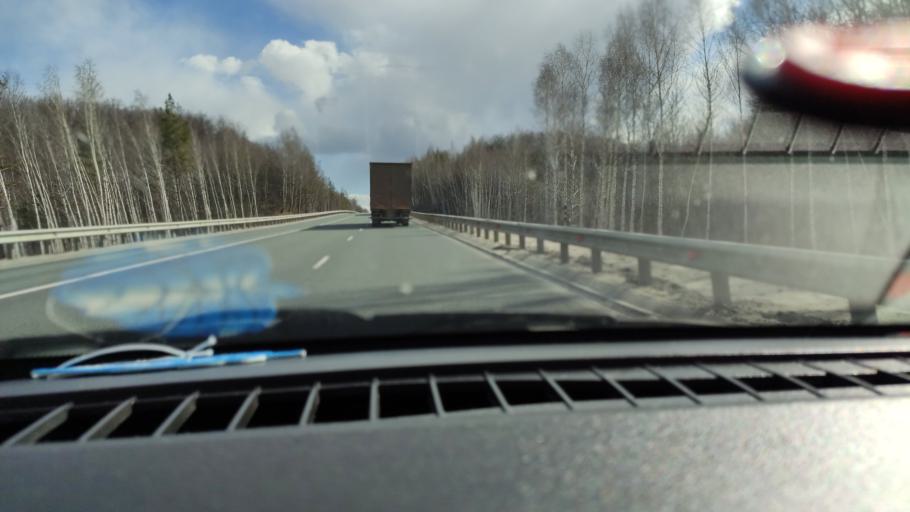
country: RU
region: Saratov
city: Khvalynsk
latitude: 52.4962
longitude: 48.0144
